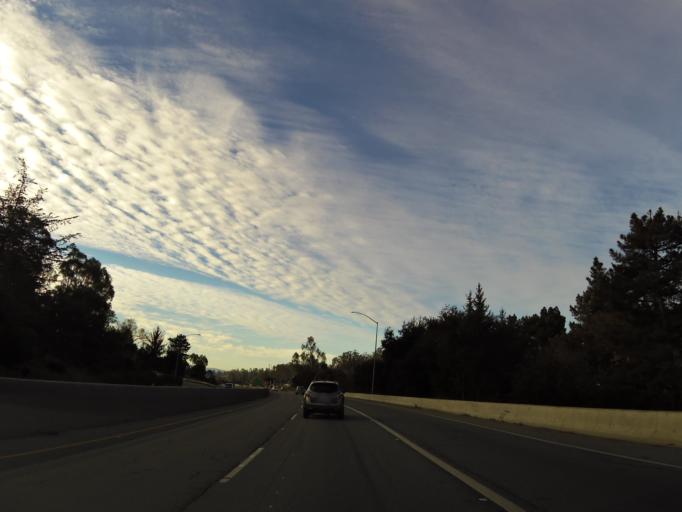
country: US
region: California
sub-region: Monterey County
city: Prunedale
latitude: 36.7990
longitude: -121.6647
